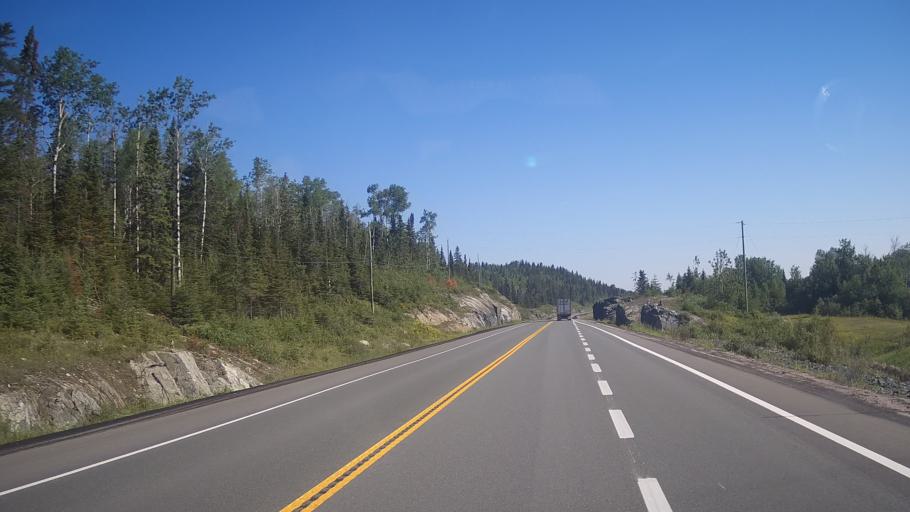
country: CA
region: Ontario
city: Dryden
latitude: 49.6200
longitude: -92.4438
